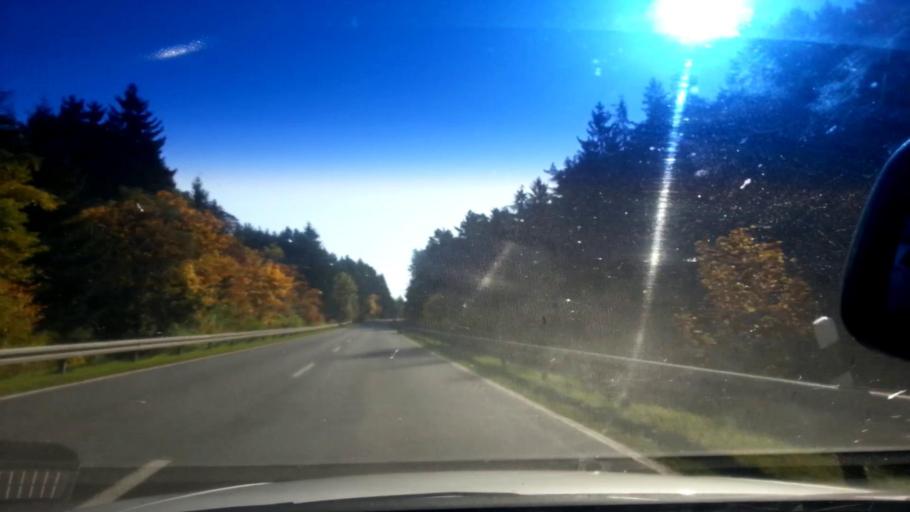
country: DE
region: Bavaria
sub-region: Upper Franconia
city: Stadelhofen
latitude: 49.9770
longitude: 11.2451
